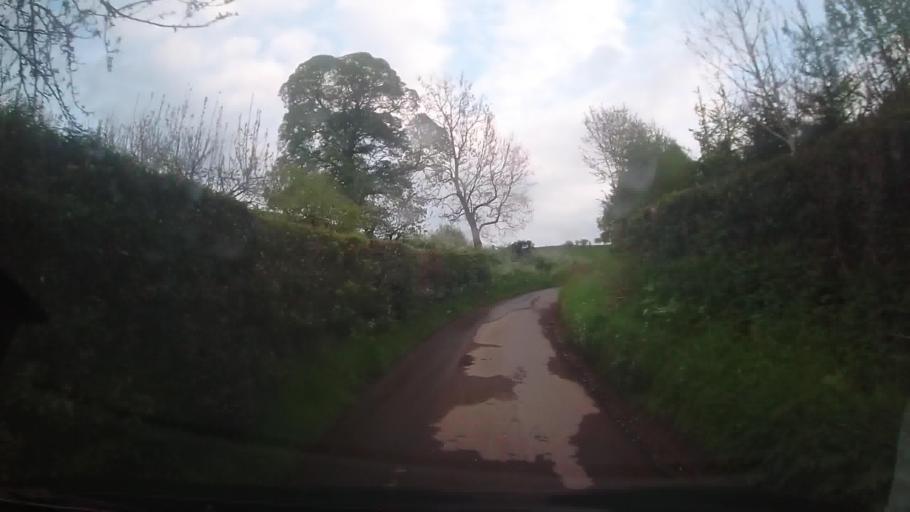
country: GB
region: England
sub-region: Shropshire
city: Ellesmere
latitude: 52.9444
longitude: -2.8676
